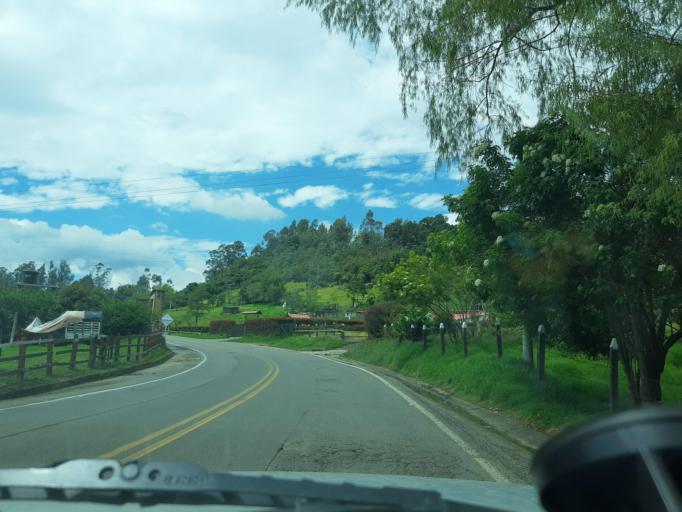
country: CO
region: Boyaca
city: Chiquinquira
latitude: 5.6221
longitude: -73.7511
